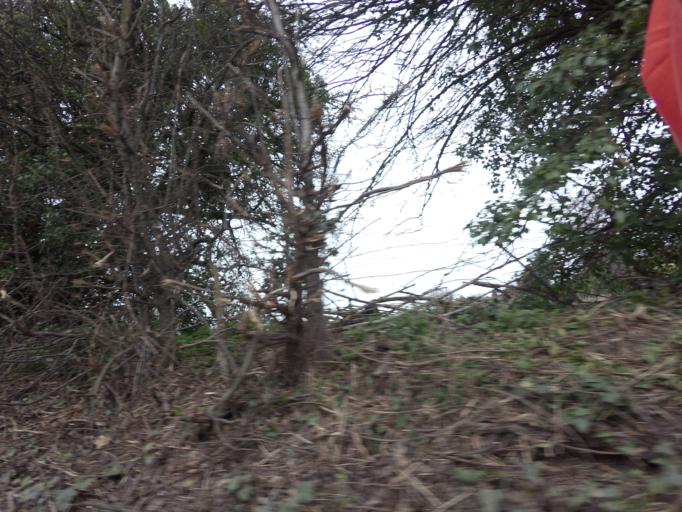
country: GB
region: England
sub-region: Kent
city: Swanley
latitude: 51.3830
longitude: 0.1560
